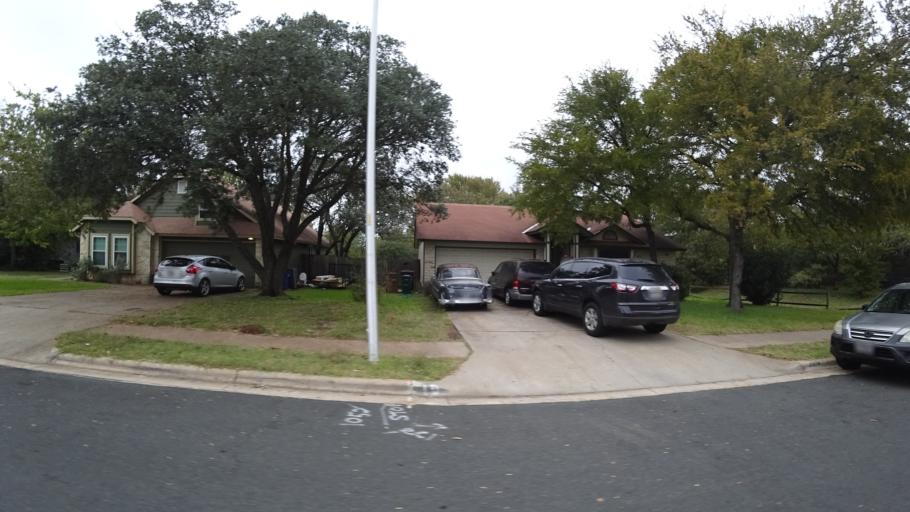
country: US
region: Texas
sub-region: Travis County
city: Shady Hollow
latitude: 30.2020
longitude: -97.8450
